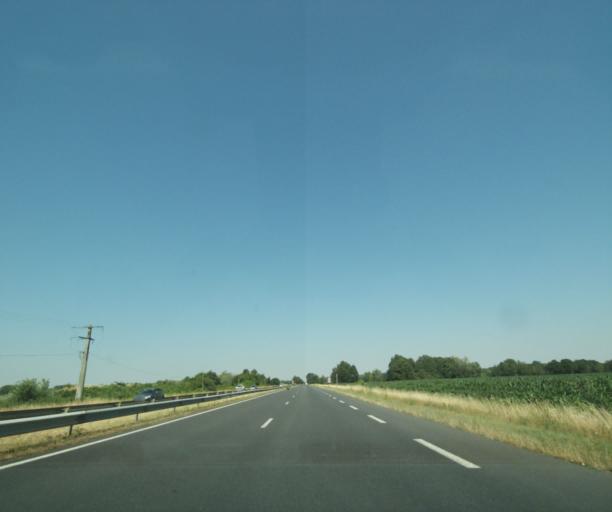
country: FR
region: Champagne-Ardenne
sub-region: Departement de la Haute-Marne
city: Villiers-en-Lieu
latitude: 48.6666
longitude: 4.7895
